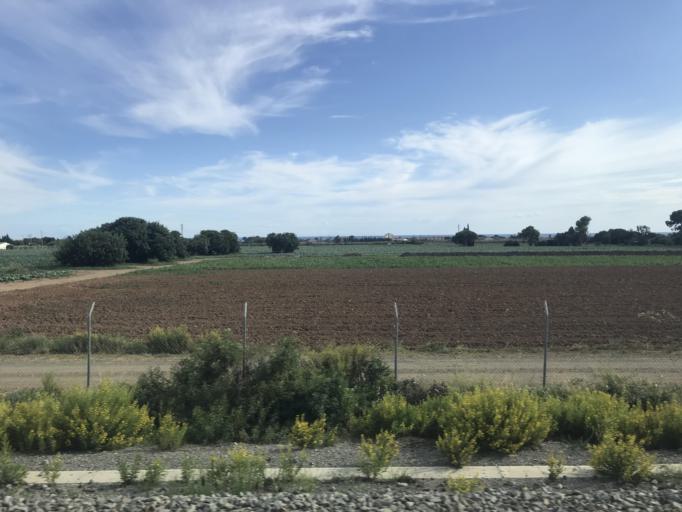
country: ES
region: Catalonia
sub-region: Provincia de Tarragona
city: Cambrils
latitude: 41.0726
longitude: 1.0188
